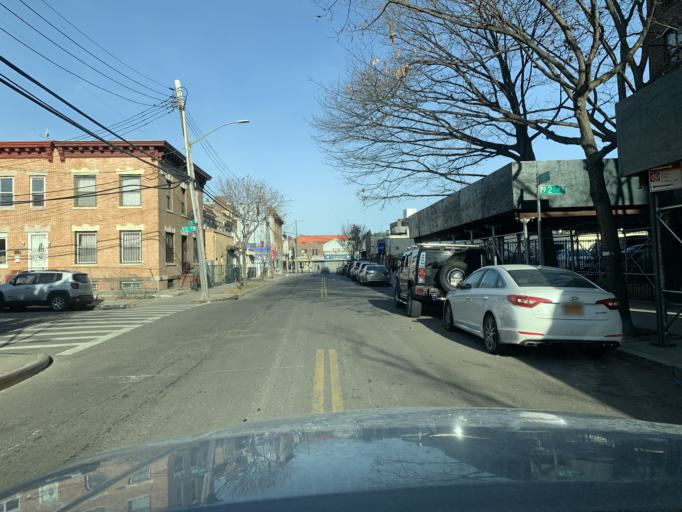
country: US
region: New York
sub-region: Queens County
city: Jamaica
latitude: 40.7061
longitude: -73.7891
